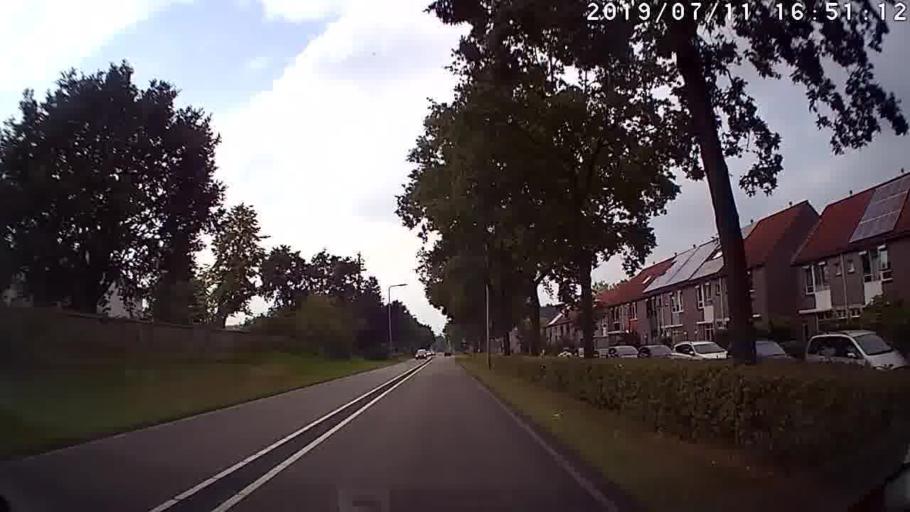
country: NL
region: Overijssel
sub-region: Gemeente Zwolle
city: Zwolle
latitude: 52.4815
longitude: 6.1182
